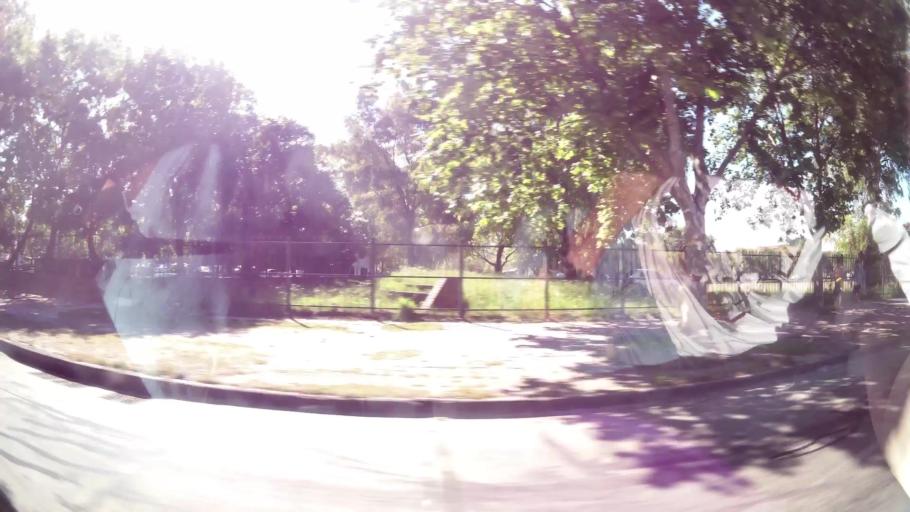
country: AR
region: Buenos Aires F.D.
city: Villa Lugano
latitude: -34.6819
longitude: -58.4527
